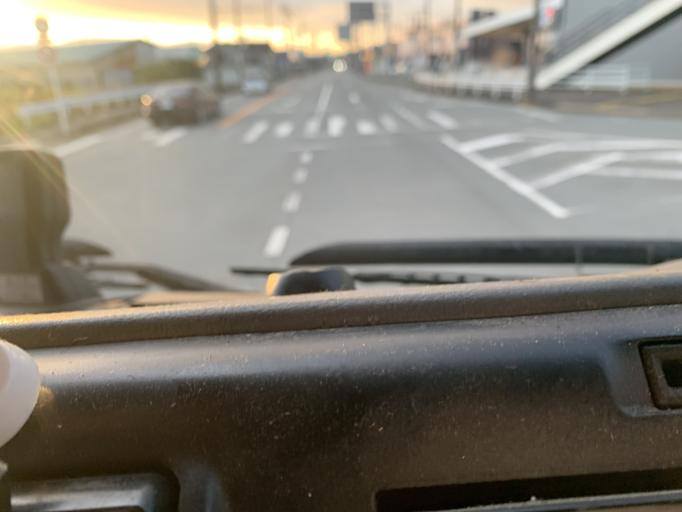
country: JP
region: Mie
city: Hisai-motomachi
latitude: 34.5763
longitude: 136.5422
